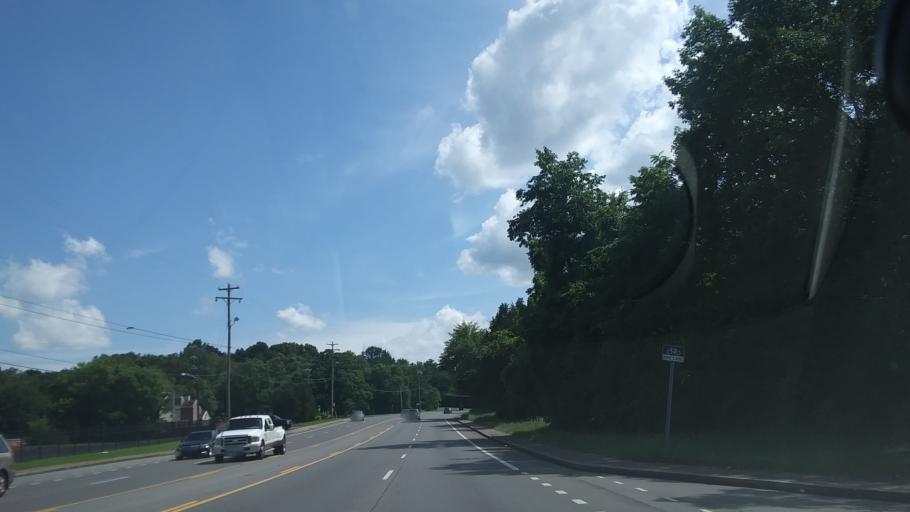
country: US
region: Tennessee
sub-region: Rutherford County
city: La Vergne
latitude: 36.0649
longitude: -86.6371
